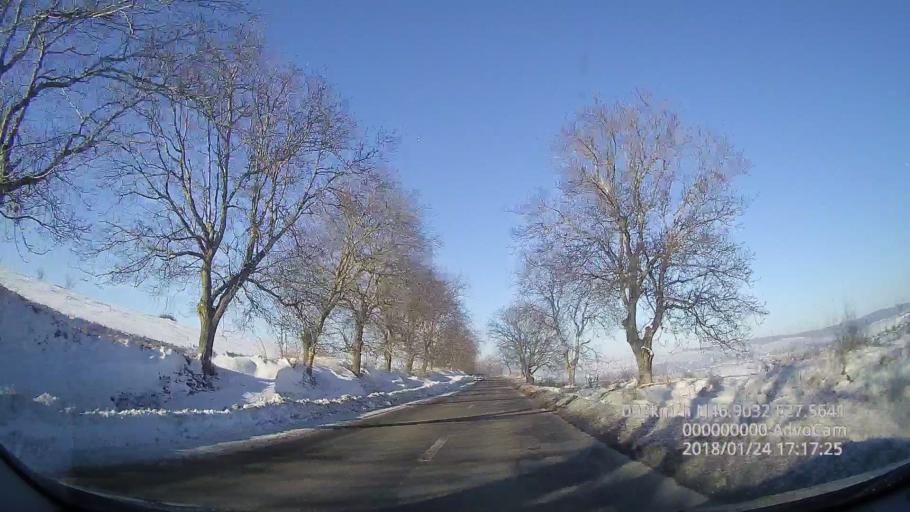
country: RO
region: Iasi
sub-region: Comuna Scanteia
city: Scanteia
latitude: 46.9038
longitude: 27.5642
